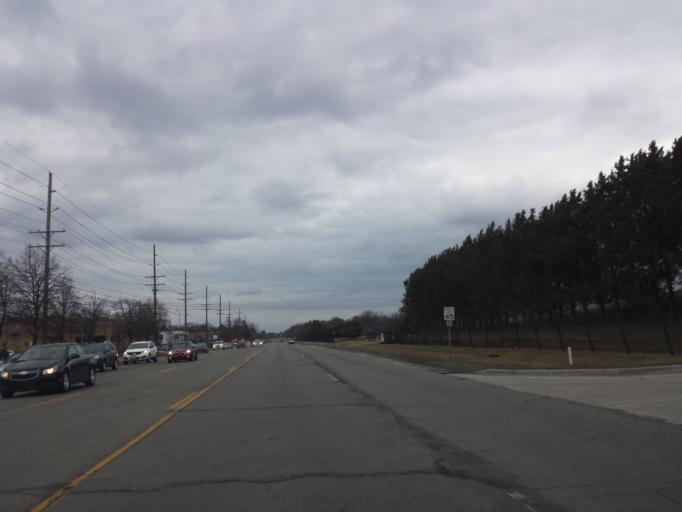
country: US
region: Michigan
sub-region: Oakland County
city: Beverly Hills
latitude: 42.5184
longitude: -83.2234
